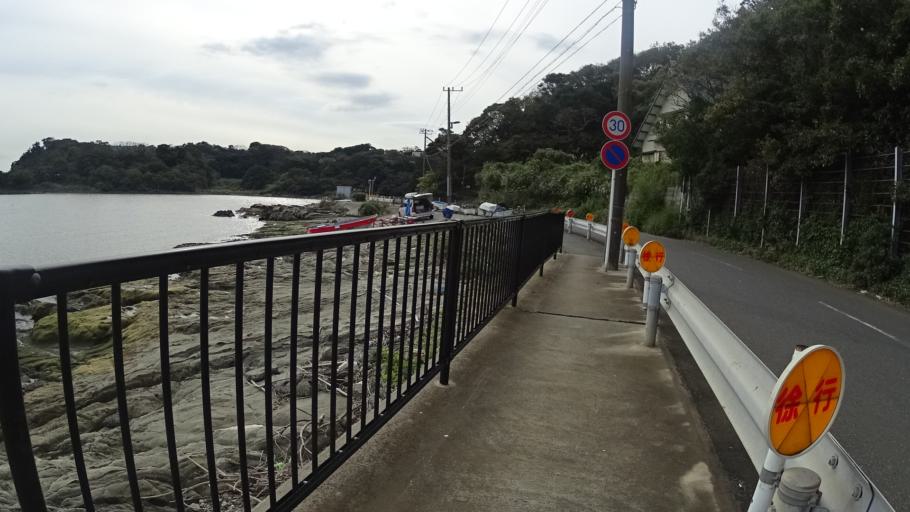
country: JP
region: Kanagawa
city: Miura
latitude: 35.1451
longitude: 139.6644
